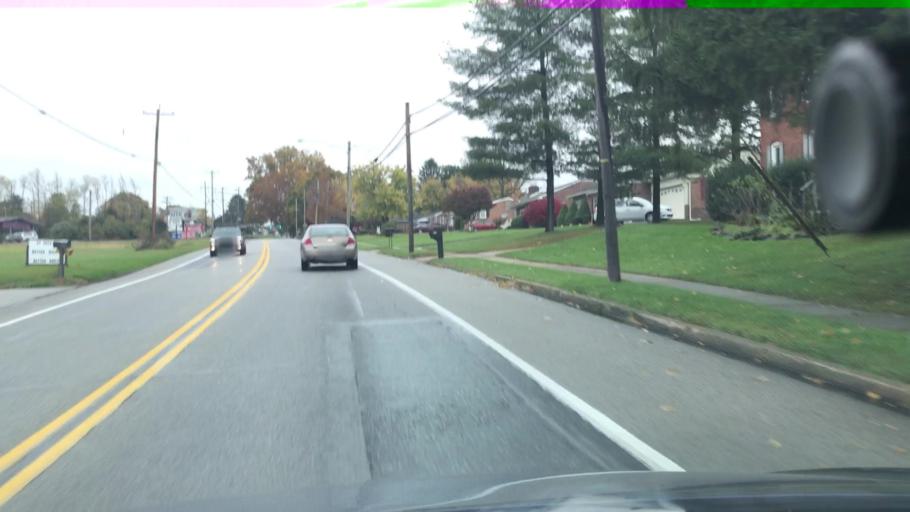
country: US
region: Pennsylvania
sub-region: York County
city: Spring Grove
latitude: 39.9077
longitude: -76.8439
